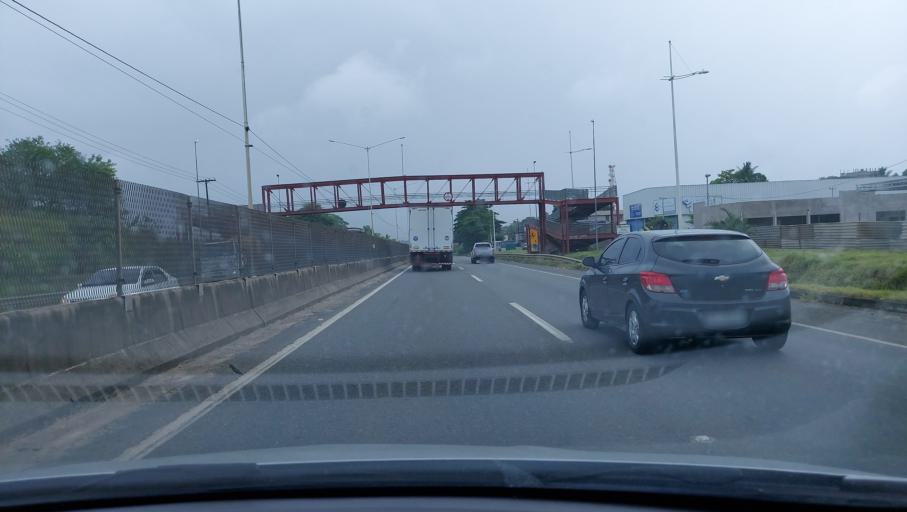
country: BR
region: Bahia
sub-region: Salvador
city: Salvador
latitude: -12.8879
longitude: -38.4409
